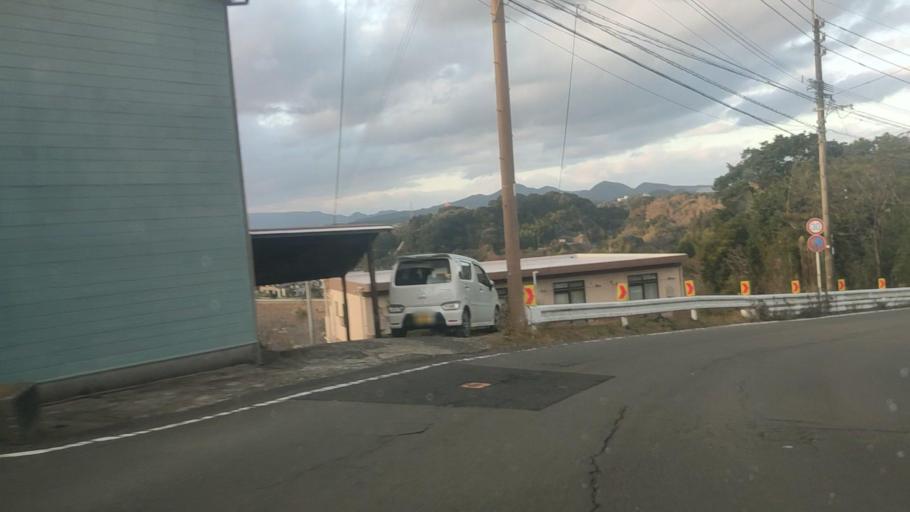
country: JP
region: Kagoshima
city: Kagoshima-shi
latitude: 31.6255
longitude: 130.5515
